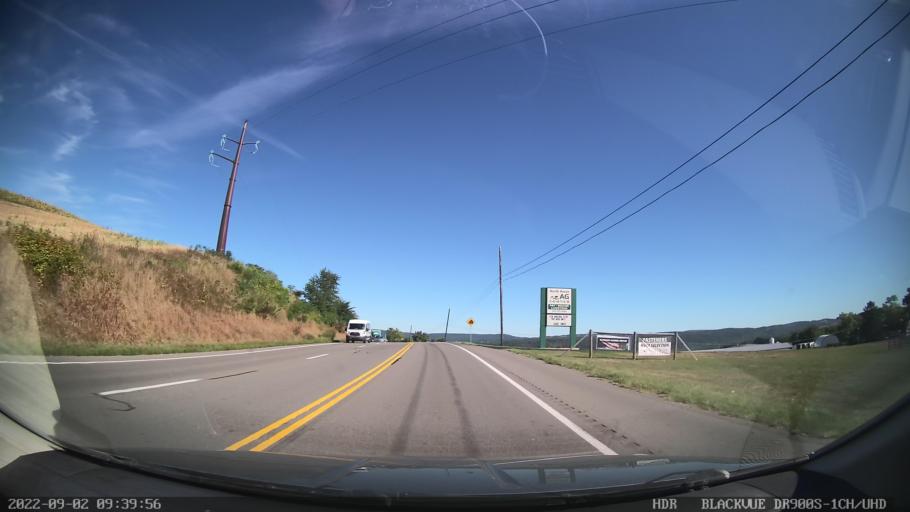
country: US
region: Pennsylvania
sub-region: Montour County
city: Mechanicsville
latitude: 40.9193
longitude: -76.5859
